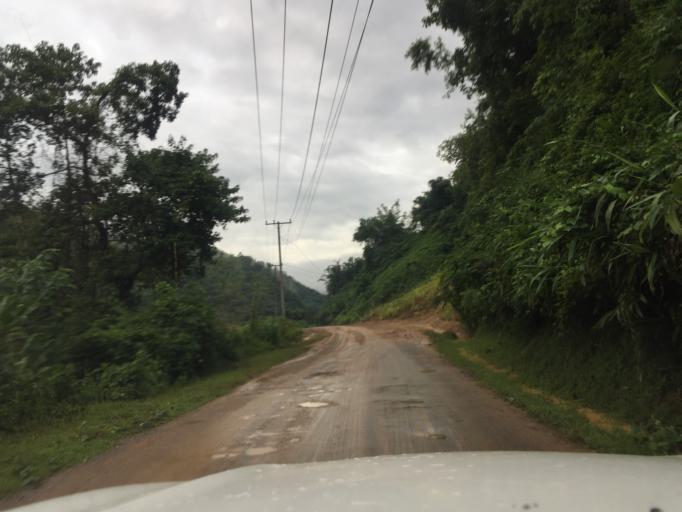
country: LA
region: Oudomxai
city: Muang La
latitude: 20.9171
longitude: 102.2000
